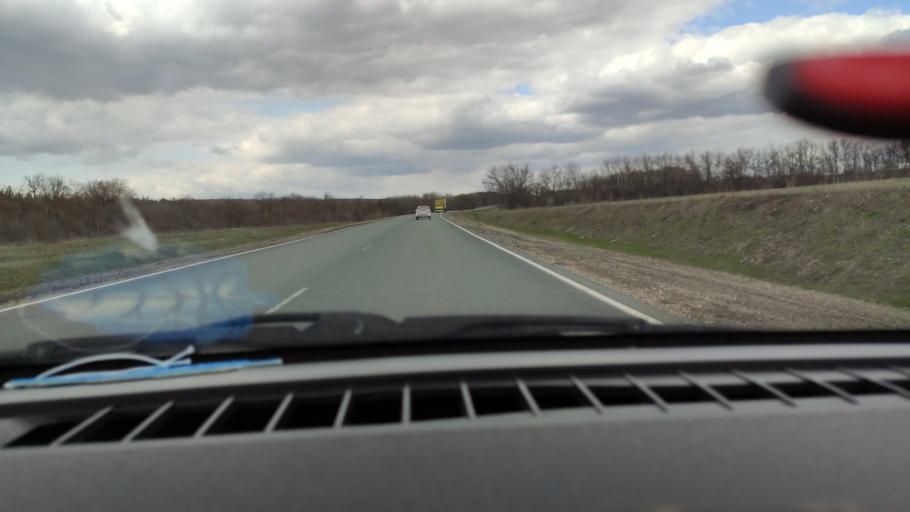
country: RU
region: Saratov
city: Tersa
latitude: 52.1028
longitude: 47.4527
